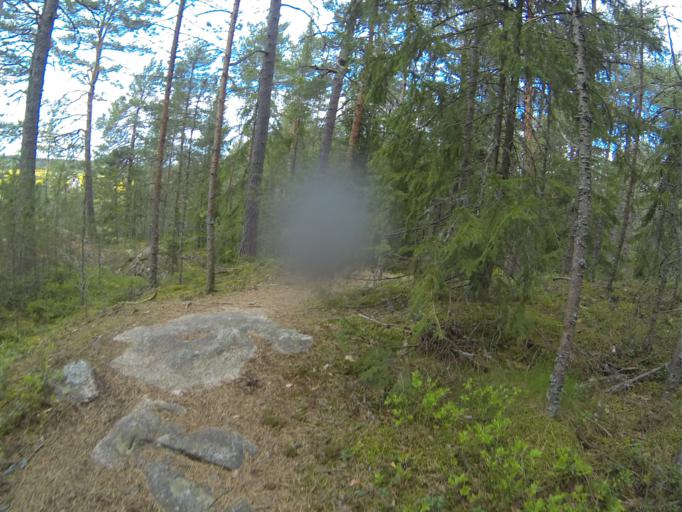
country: FI
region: Varsinais-Suomi
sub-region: Salo
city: Salo
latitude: 60.3545
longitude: 23.1113
